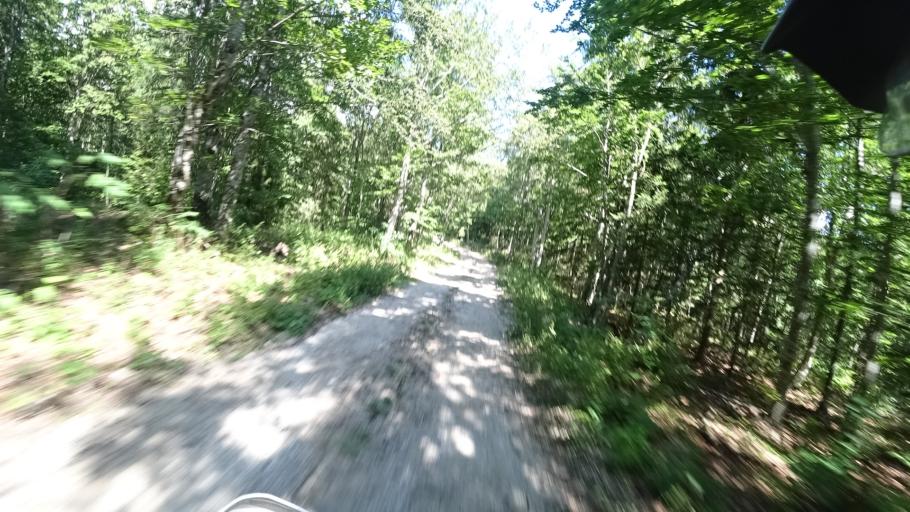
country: BA
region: Federation of Bosnia and Herzegovina
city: Orasac
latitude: 44.5034
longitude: 15.9546
